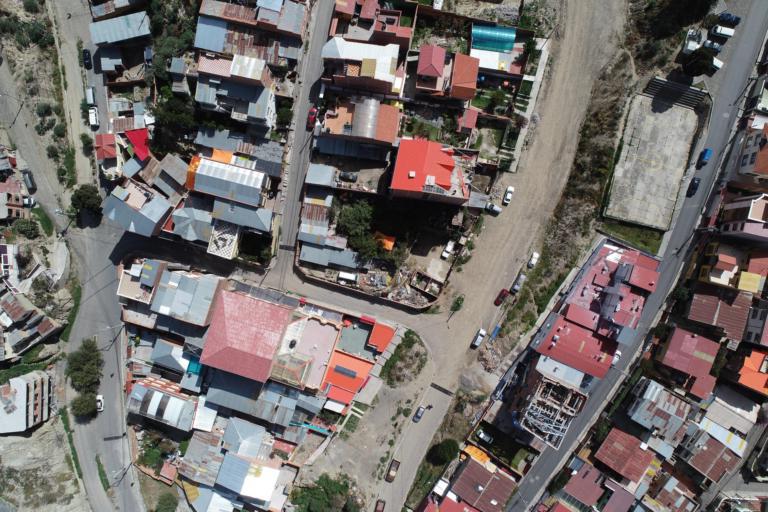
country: BO
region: La Paz
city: La Paz
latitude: -16.5191
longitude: -68.1043
